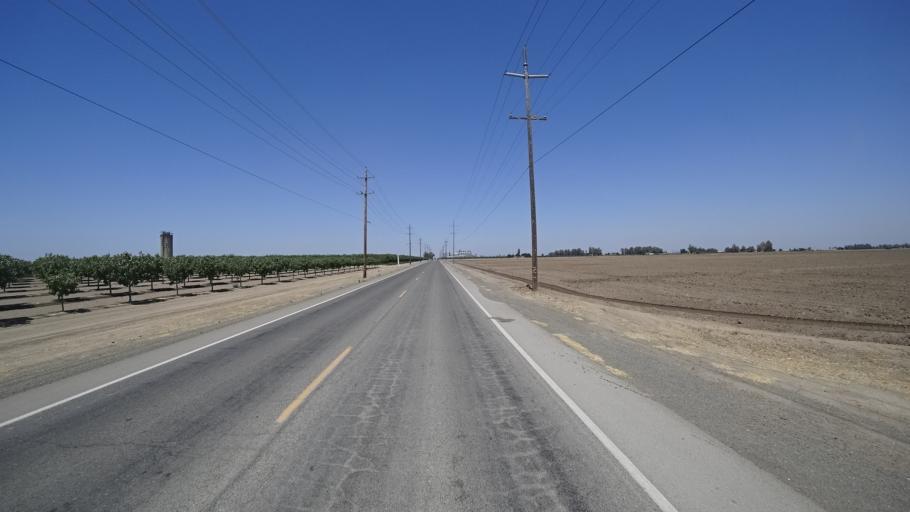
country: US
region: California
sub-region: Kings County
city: Home Garden
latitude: 36.2041
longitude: -119.6459
